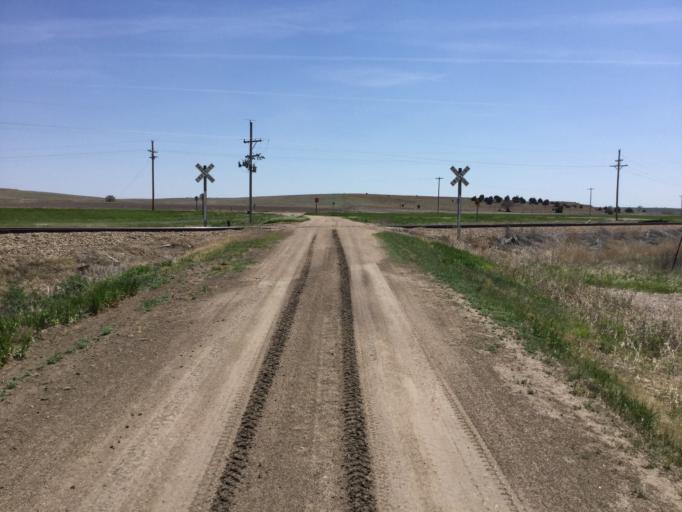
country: US
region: Kansas
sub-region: Decatur County
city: Oberlin
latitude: 39.6697
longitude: -100.3295
